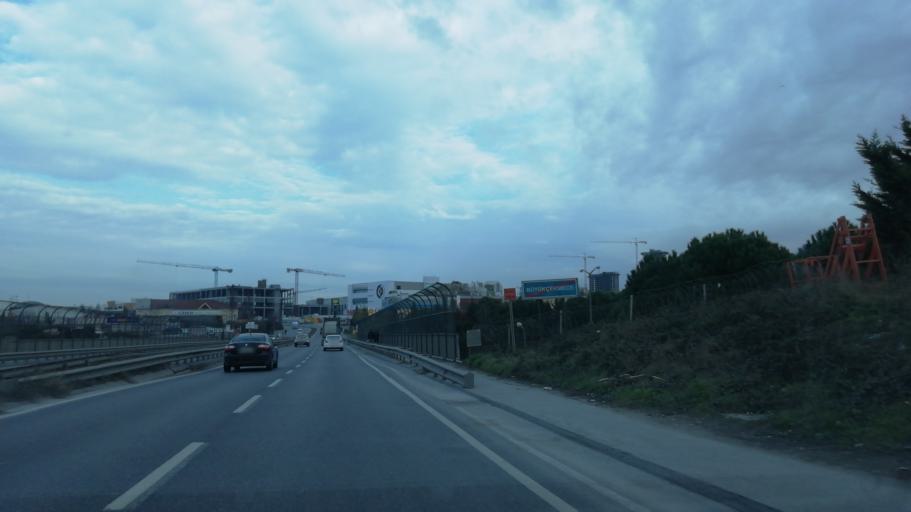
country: TR
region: Istanbul
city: Esenyurt
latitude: 41.0893
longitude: 28.6323
